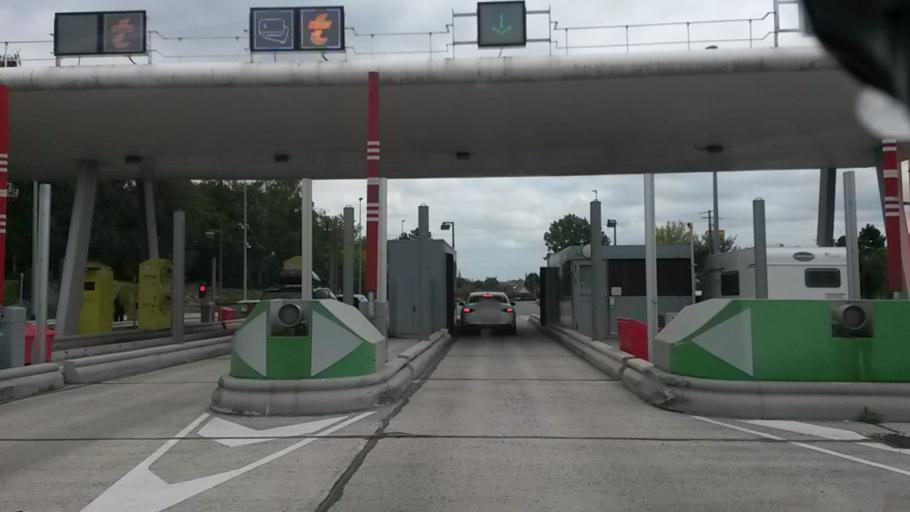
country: FR
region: Nord-Pas-de-Calais
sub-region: Departement du Nord
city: Proville
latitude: 50.1756
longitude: 3.1924
